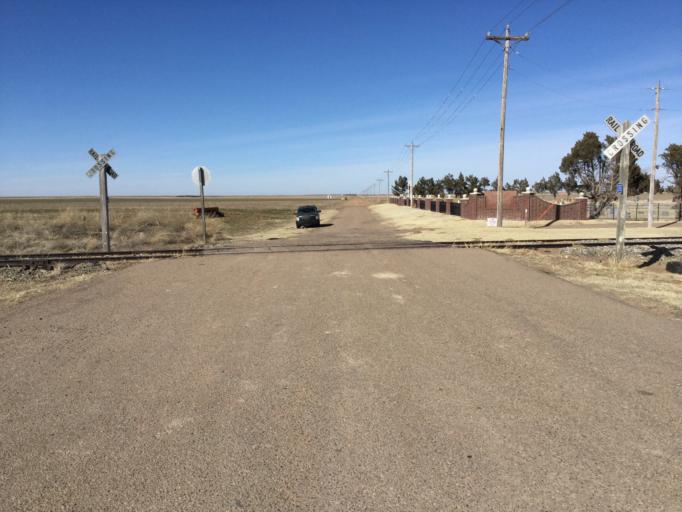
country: US
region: Kansas
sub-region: Morton County
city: Elkhart
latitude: 37.1189
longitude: -101.6460
